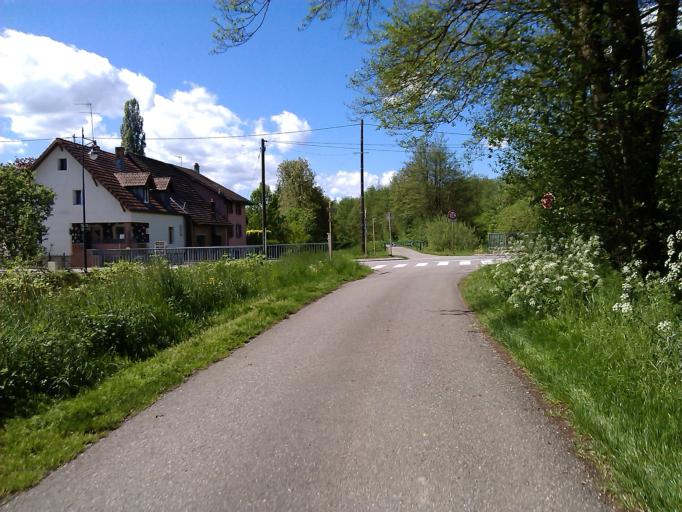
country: FR
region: Franche-Comte
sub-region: Territoire de Belfort
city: Montreux-Chateau
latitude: 47.6166
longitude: 7.0306
